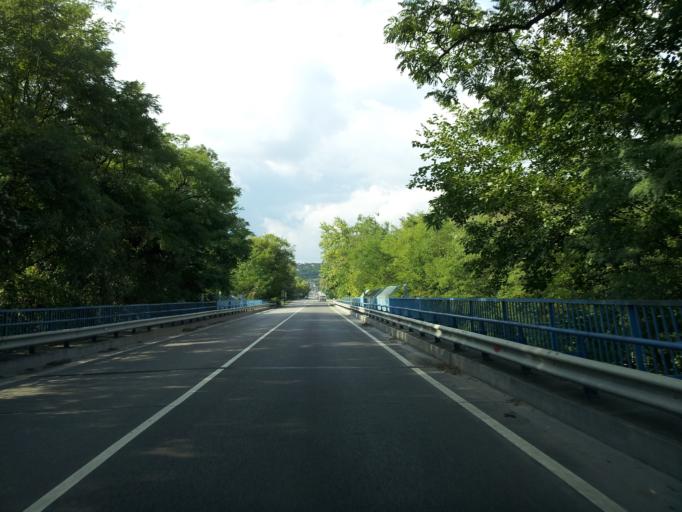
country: HU
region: Pest
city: Vac
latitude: 47.8093
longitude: 19.0945
